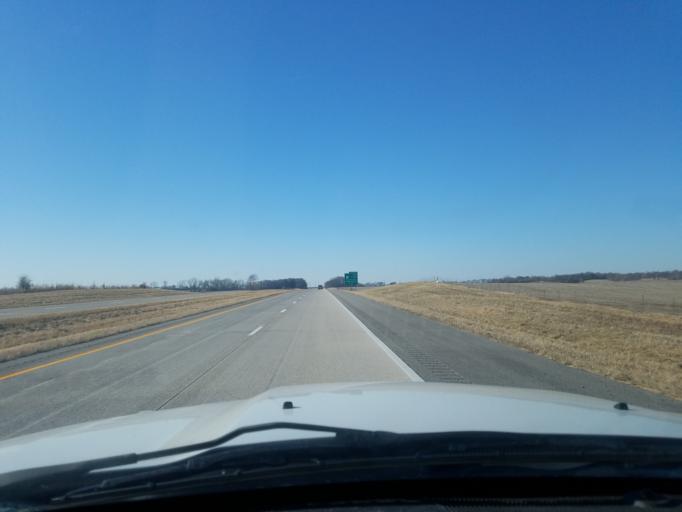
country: US
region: Kentucky
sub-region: Henderson County
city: Henderson
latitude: 37.8032
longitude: -87.5227
